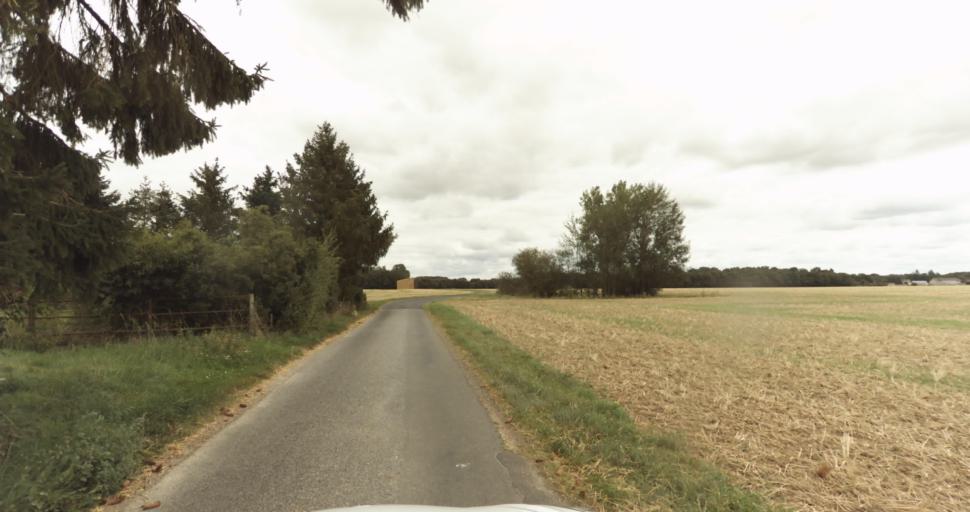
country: FR
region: Haute-Normandie
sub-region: Departement de l'Eure
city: La Madeleine-de-Nonancourt
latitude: 48.8359
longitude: 1.2023
